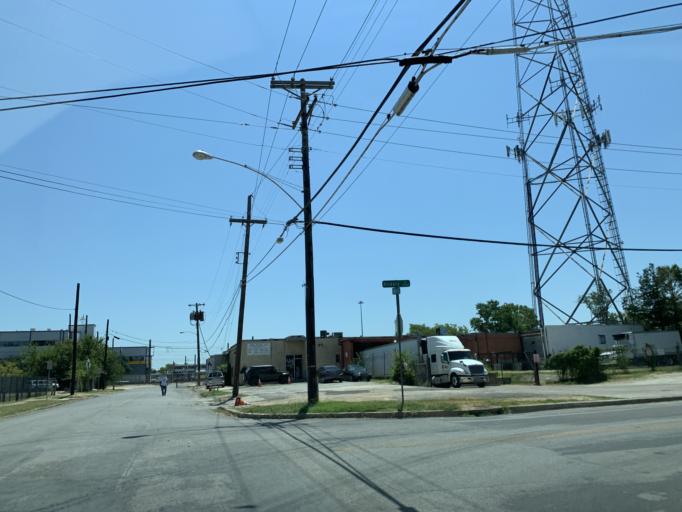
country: US
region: Texas
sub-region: Dallas County
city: Dallas
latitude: 32.7793
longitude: -96.7752
